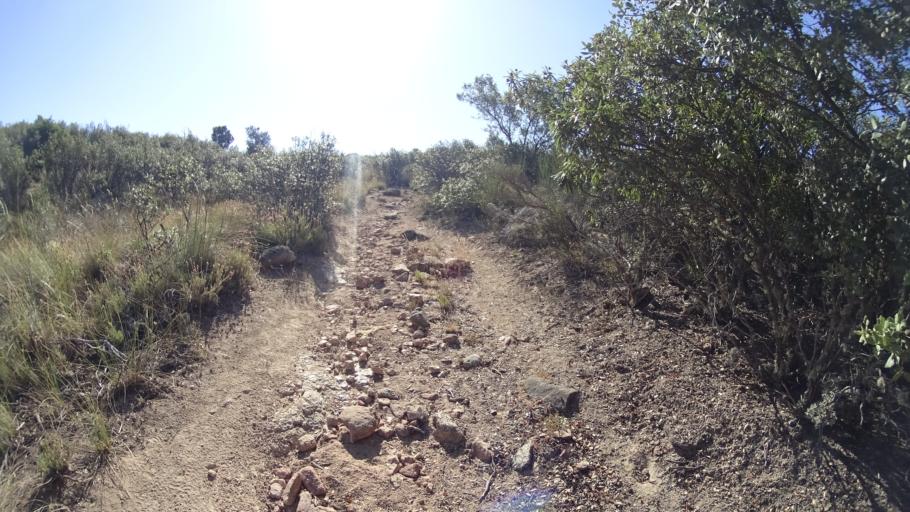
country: ES
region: Madrid
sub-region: Provincia de Madrid
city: Hoyo de Manzanares
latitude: 40.6474
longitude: -3.9372
